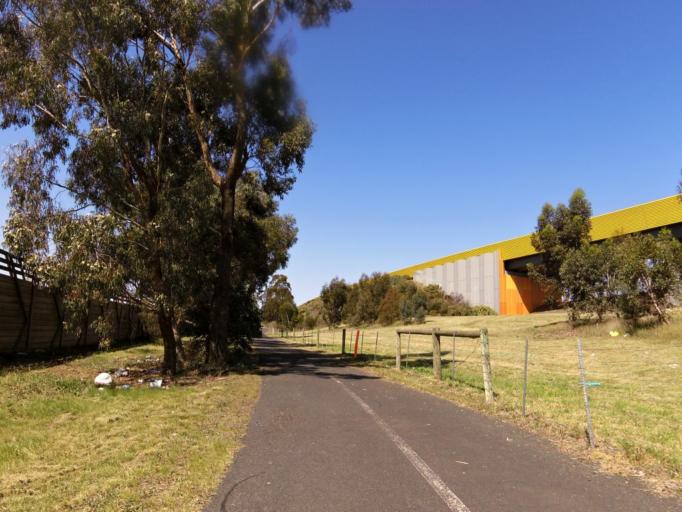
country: AU
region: Victoria
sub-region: Brimbank
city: Derrimut
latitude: -37.7985
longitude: 144.7909
